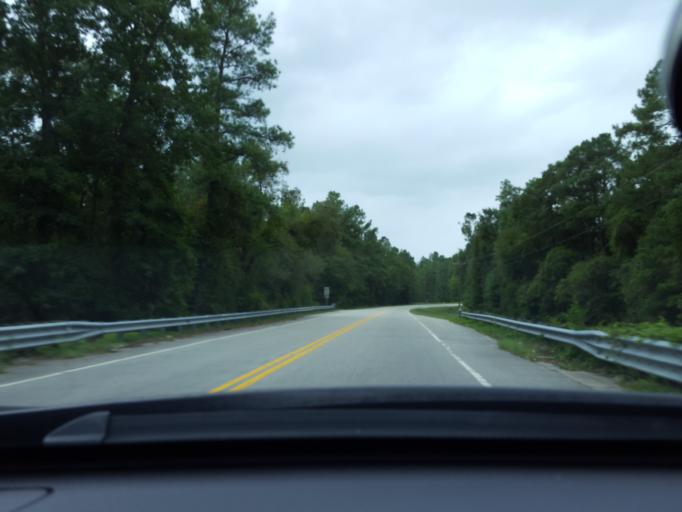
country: US
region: North Carolina
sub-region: Sampson County
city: Clinton
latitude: 34.7872
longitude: -78.3227
